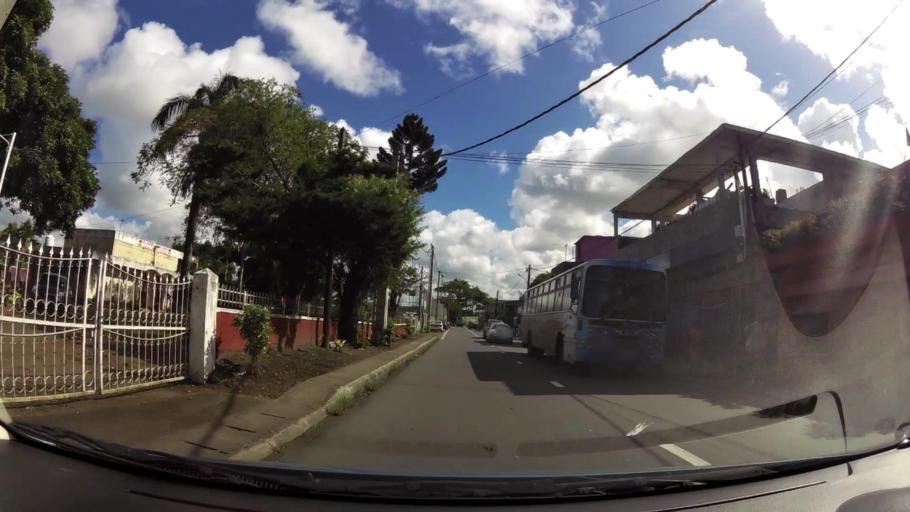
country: MU
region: Grand Port
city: Plaine Magnien
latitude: -20.4313
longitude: 57.6580
